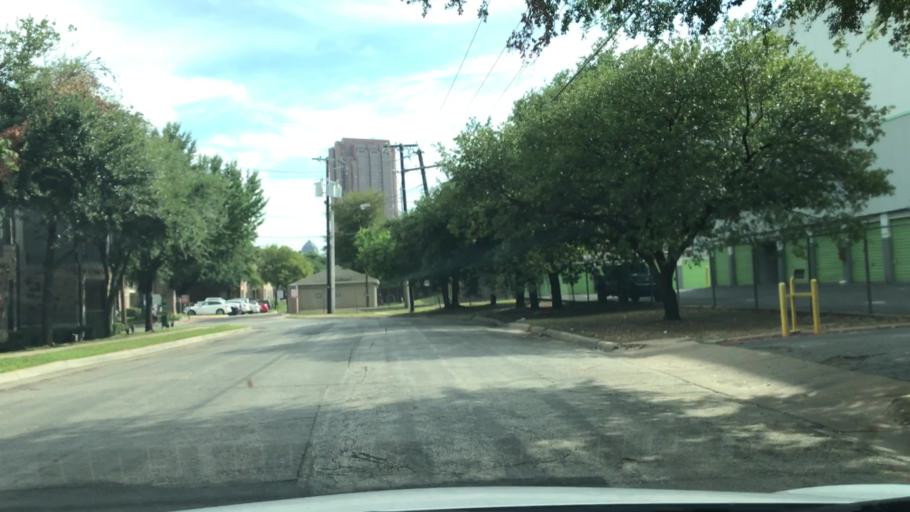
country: US
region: Texas
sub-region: Dallas County
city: Highland Park
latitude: 32.8132
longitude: -96.7885
